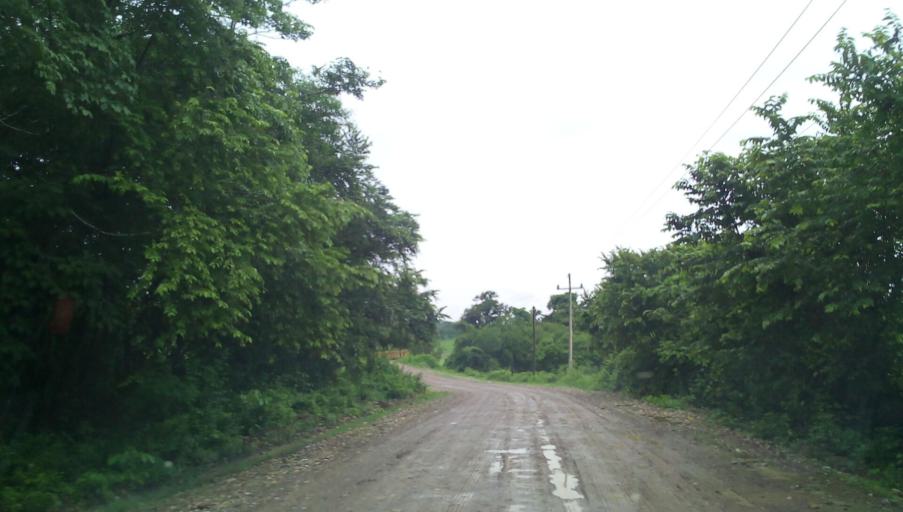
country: MX
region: Veracruz
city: Tempoal de Sanchez
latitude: 21.4353
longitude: -98.4222
